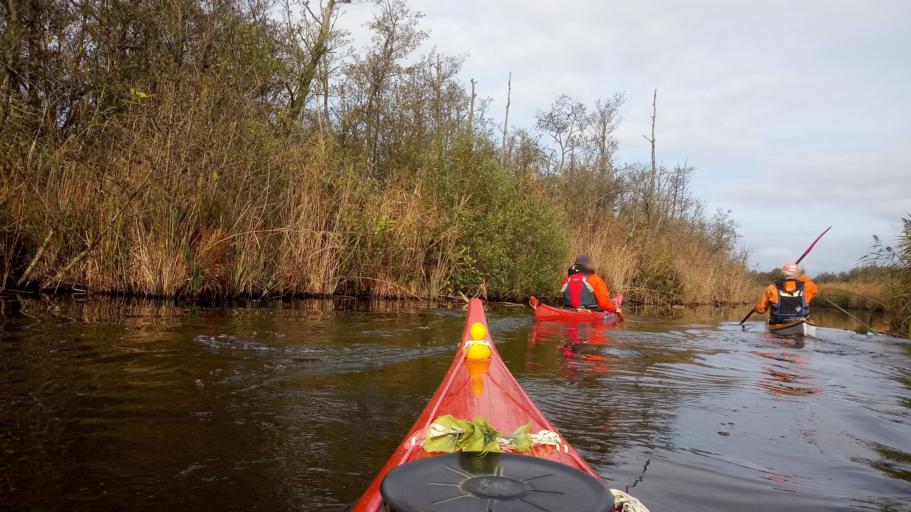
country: NL
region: Overijssel
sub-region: Gemeente Steenwijkerland
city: Sint Jansklooster
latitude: 52.6575
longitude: 6.0403
